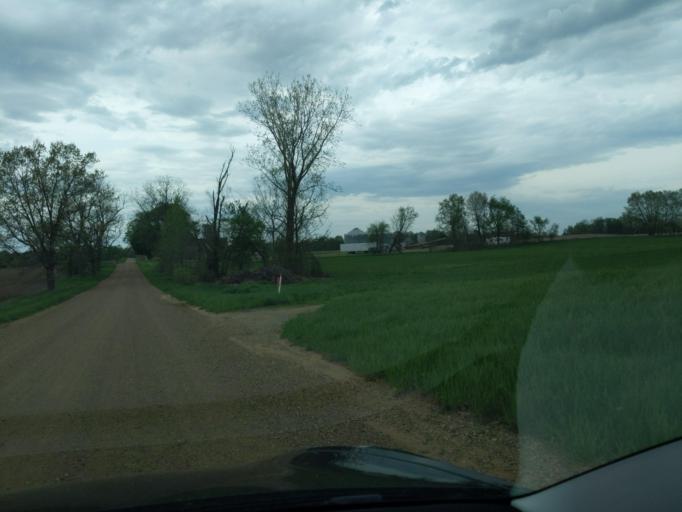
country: US
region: Michigan
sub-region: Ingham County
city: Stockbridge
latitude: 42.4187
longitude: -84.1362
